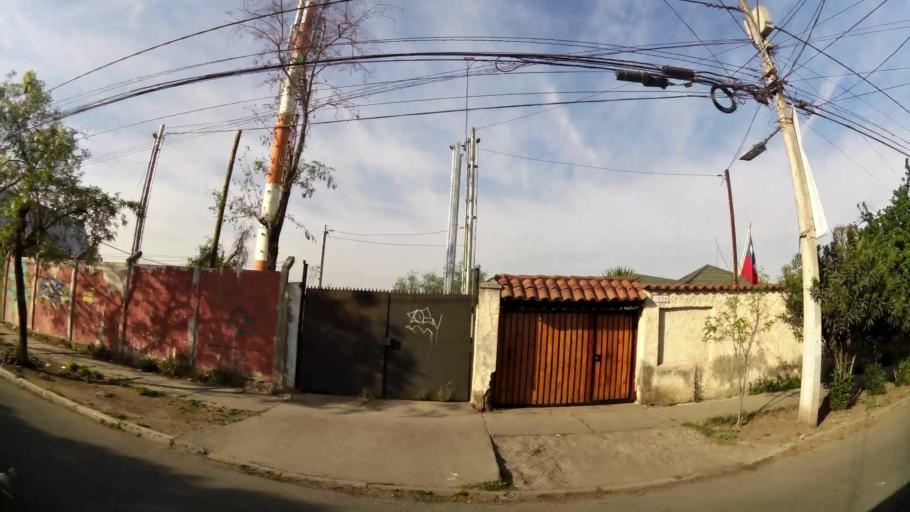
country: CL
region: Santiago Metropolitan
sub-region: Provincia de Santiago
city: Santiago
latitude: -33.5188
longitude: -70.6688
